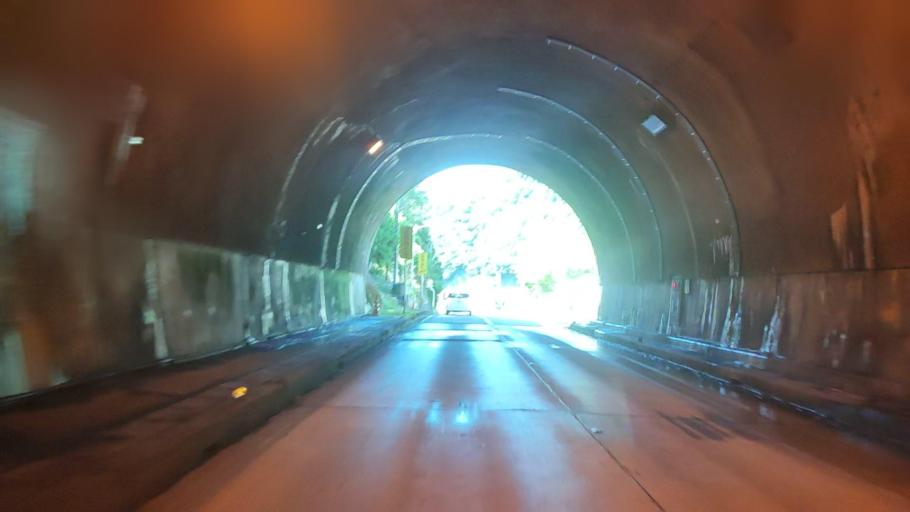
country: JP
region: Nara
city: Yoshino-cho
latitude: 34.3533
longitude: 135.9319
